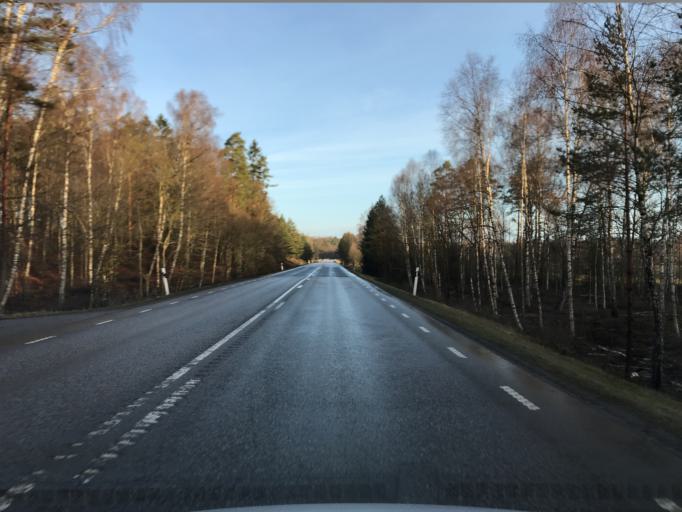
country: SE
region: Skane
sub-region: Hassleholms Kommun
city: Bjarnum
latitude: 56.2546
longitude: 13.7177
